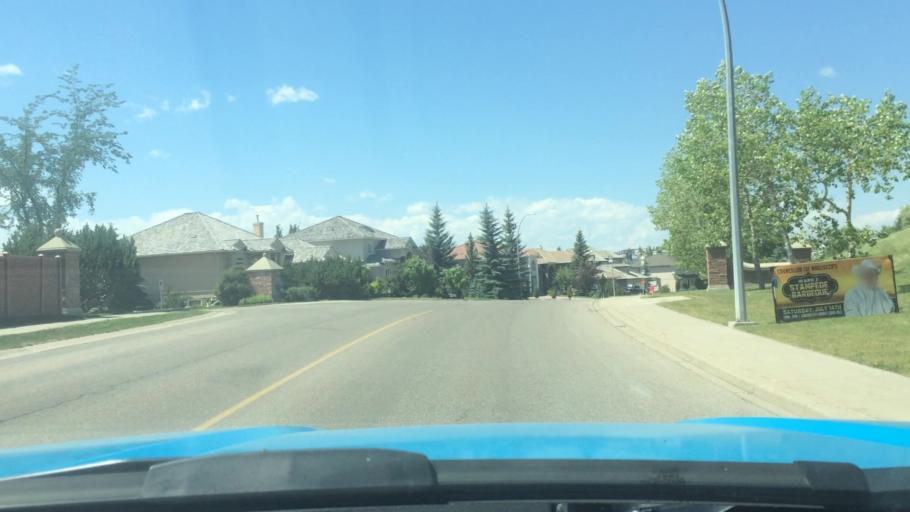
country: CA
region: Alberta
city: Calgary
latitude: 51.1329
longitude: -114.1960
